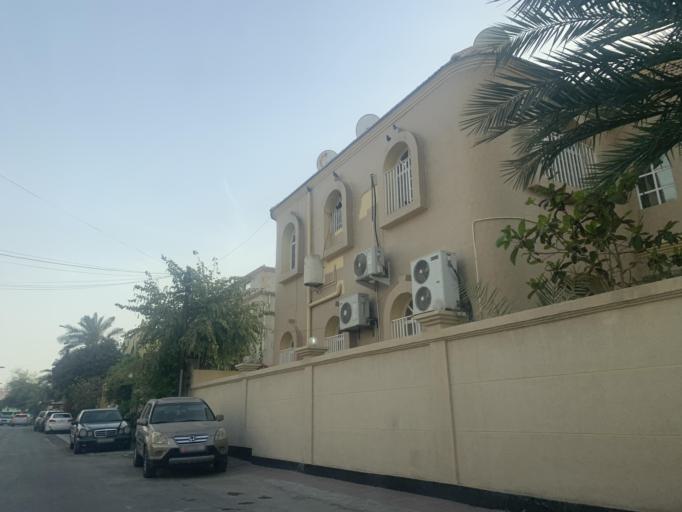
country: BH
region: Northern
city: Ar Rifa'
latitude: 26.1342
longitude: 50.5552
